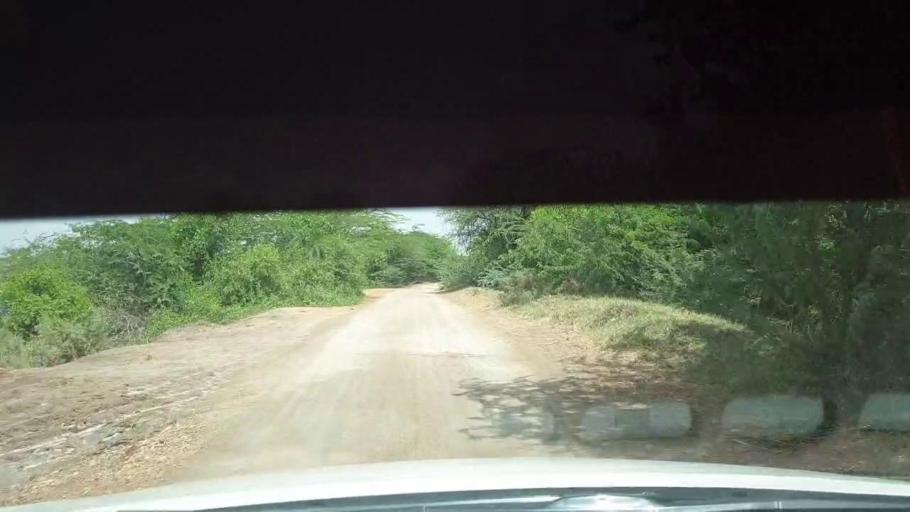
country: PK
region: Sindh
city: Kadhan
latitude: 24.5141
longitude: 68.9740
